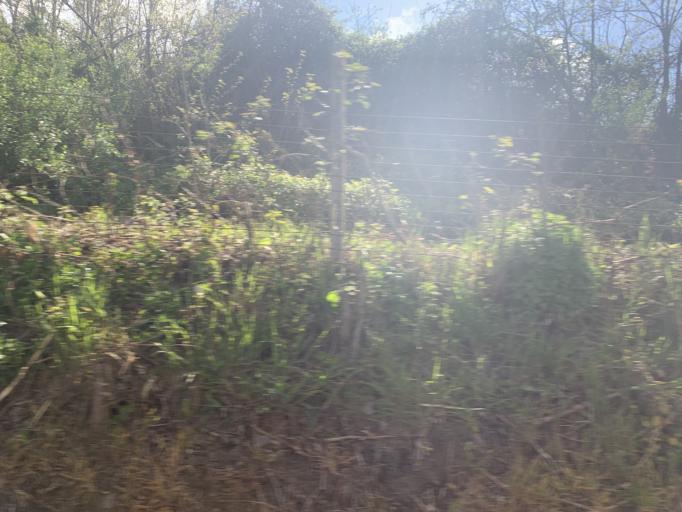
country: IT
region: Latium
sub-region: Citta metropolitana di Roma Capitale
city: Marino
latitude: 41.7770
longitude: 12.6511
